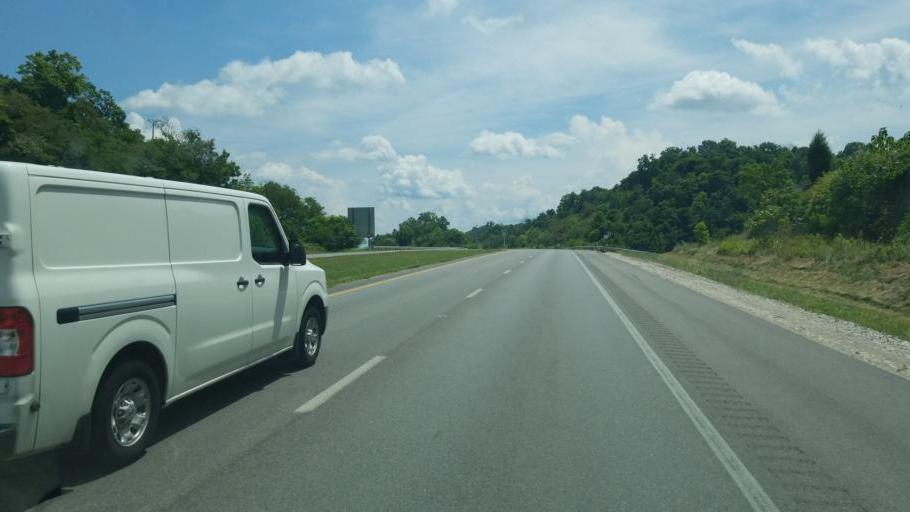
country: US
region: West Virginia
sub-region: Mason County
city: Point Pleasant
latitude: 38.8250
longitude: -82.1275
